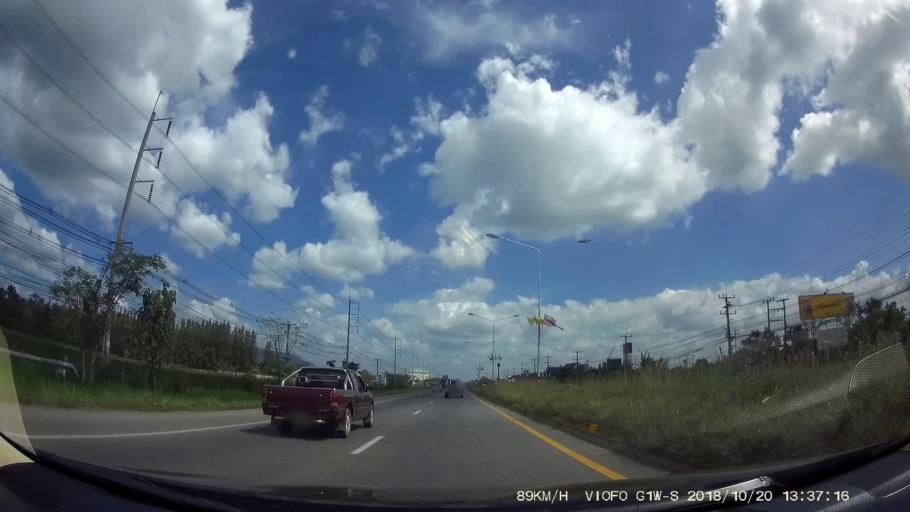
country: TH
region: Khon Kaen
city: Chum Phae
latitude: 16.5590
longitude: 102.0686
